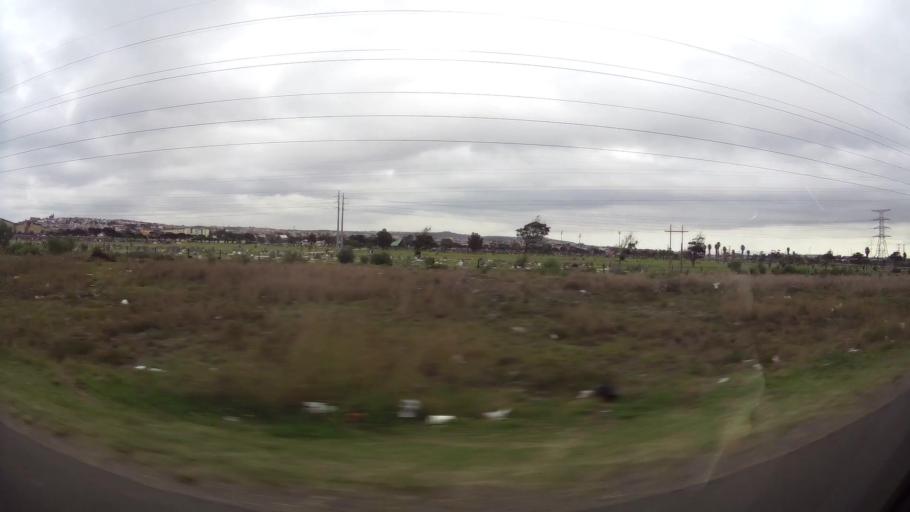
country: ZA
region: Eastern Cape
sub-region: Nelson Mandela Bay Metropolitan Municipality
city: Port Elizabeth
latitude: -33.9187
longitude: 25.5691
